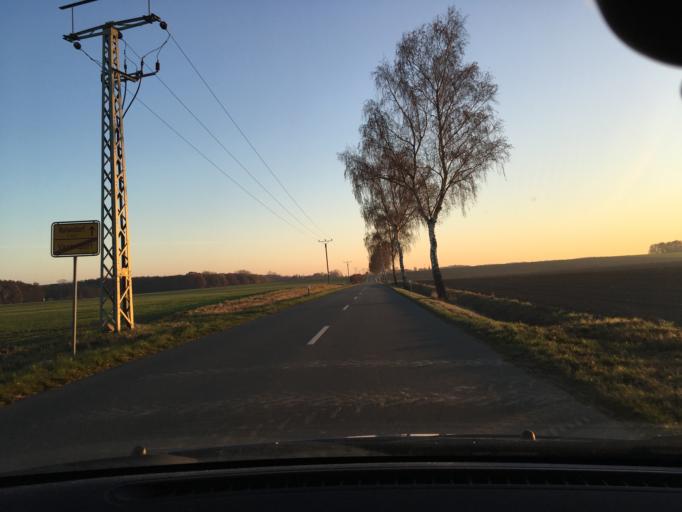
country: DE
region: Lower Saxony
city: Natendorf
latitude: 53.0953
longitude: 10.4674
